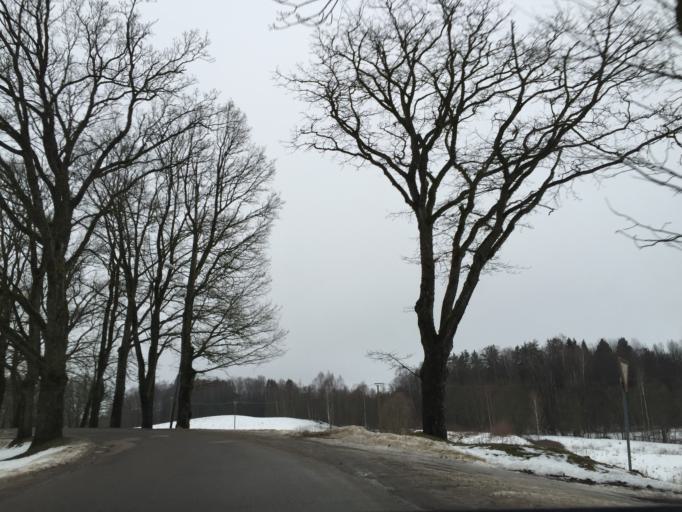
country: LV
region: Krimulda
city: Ragana
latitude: 57.1586
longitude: 24.7016
